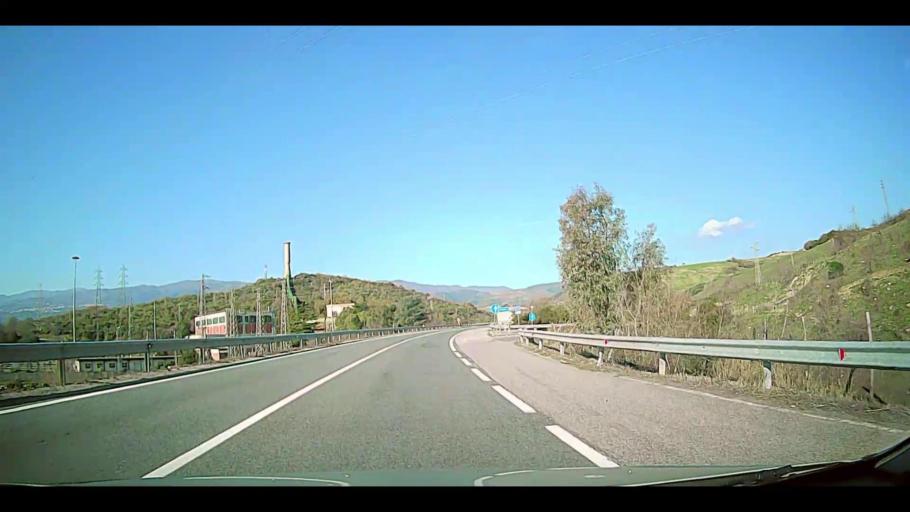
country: IT
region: Calabria
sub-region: Provincia di Crotone
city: Roccabernarda
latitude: 39.1848
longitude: 16.8359
